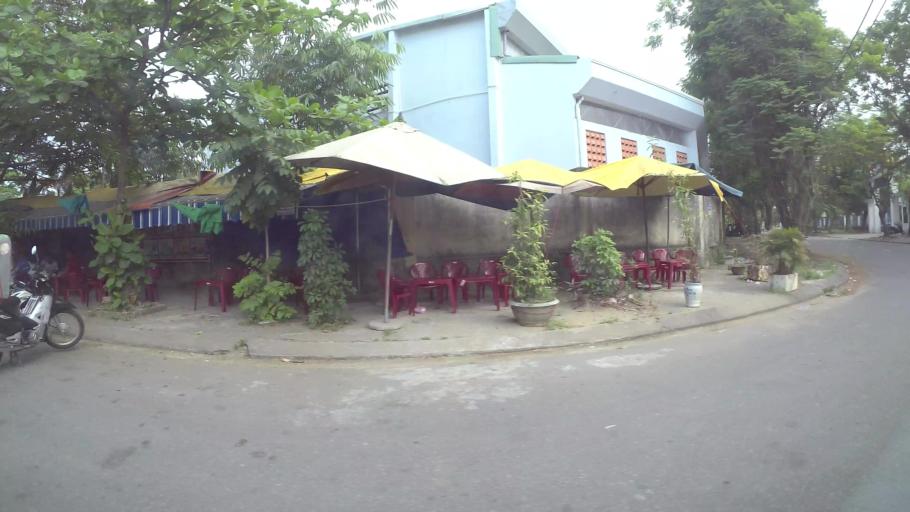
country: VN
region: Da Nang
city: Lien Chieu
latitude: 16.0577
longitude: 108.1618
